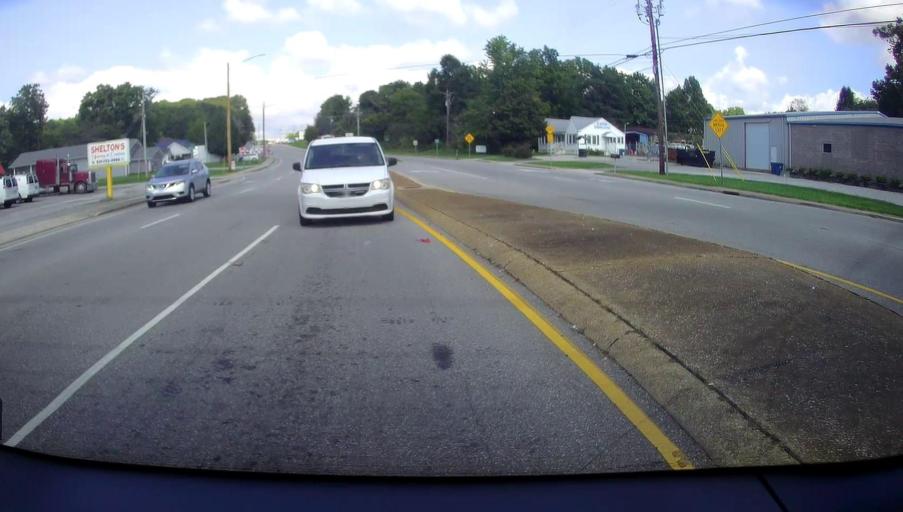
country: US
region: Tennessee
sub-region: Coffee County
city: Manchester
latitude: 35.4878
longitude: -86.0920
